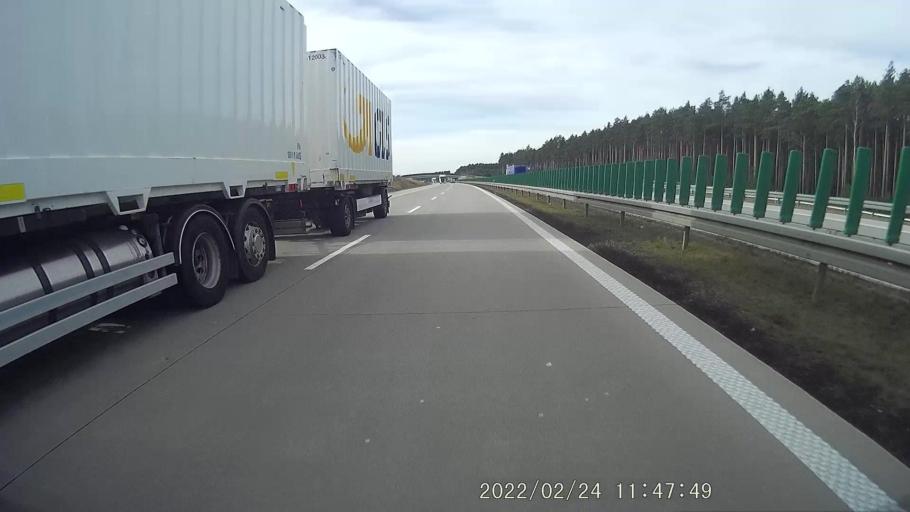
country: PL
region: Lower Silesian Voivodeship
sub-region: Powiat polkowicki
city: Radwanice
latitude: 51.5784
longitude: 15.9527
